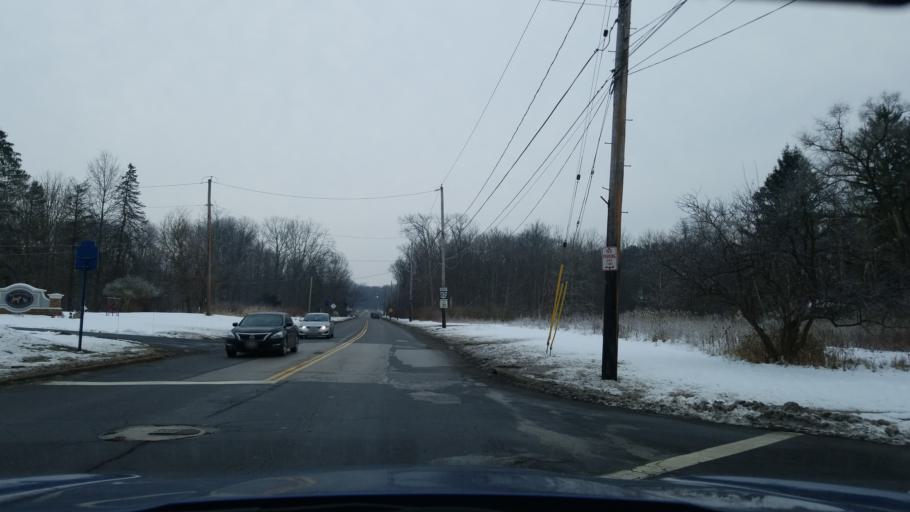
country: US
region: Ohio
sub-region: Cuyahoga County
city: Brecksville
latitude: 41.3221
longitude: -81.5926
